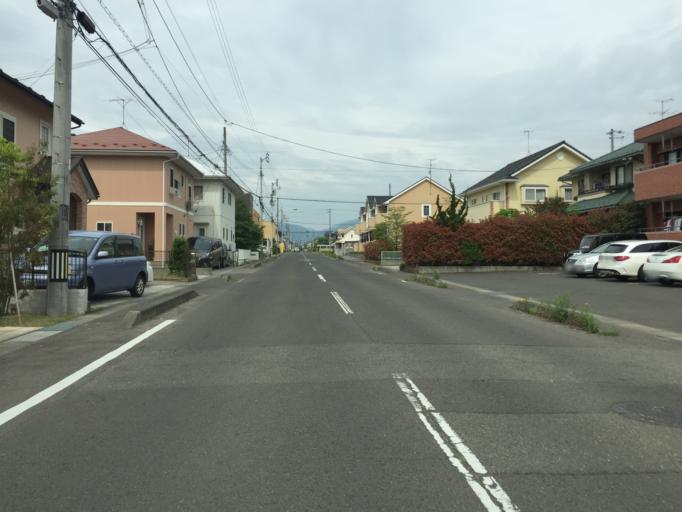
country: JP
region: Fukushima
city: Fukushima-shi
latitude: 37.7877
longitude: 140.4487
